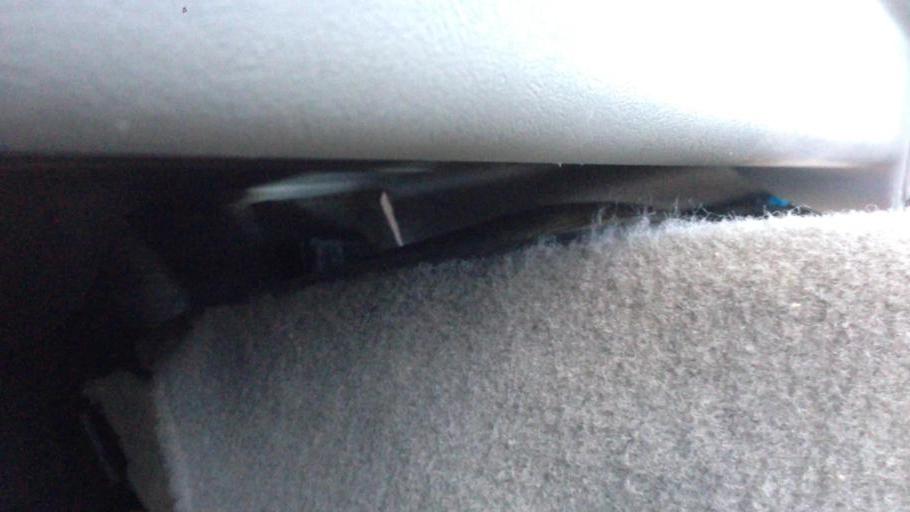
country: US
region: New York
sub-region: Columbia County
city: Lorenz Park
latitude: 42.2786
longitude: -73.7617
